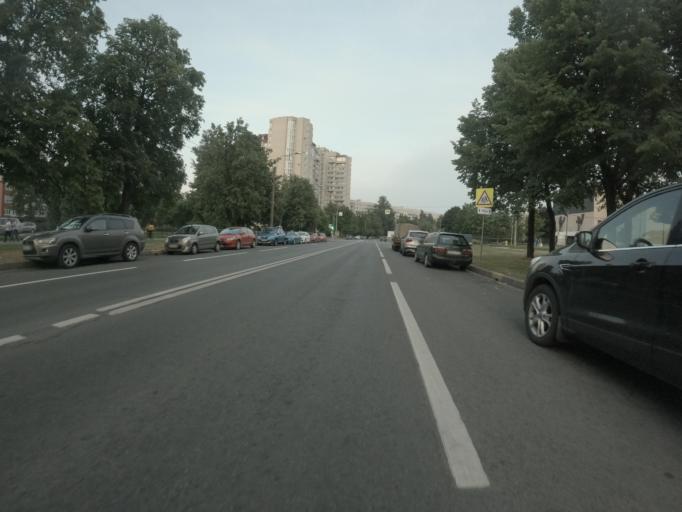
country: RU
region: St.-Petersburg
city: Krasnogvargeisky
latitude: 59.9673
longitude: 30.4290
